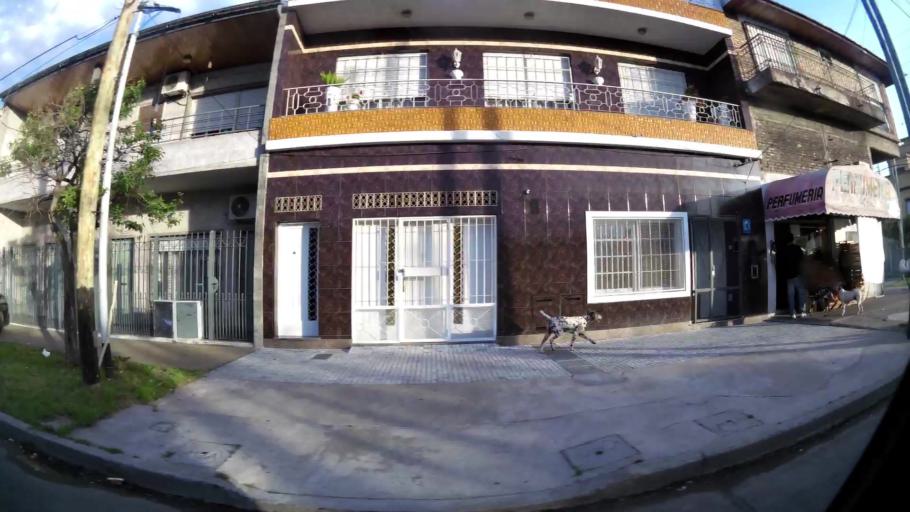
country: AR
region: Buenos Aires
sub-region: Partido de Avellaneda
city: Avellaneda
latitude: -34.7005
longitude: -58.3376
